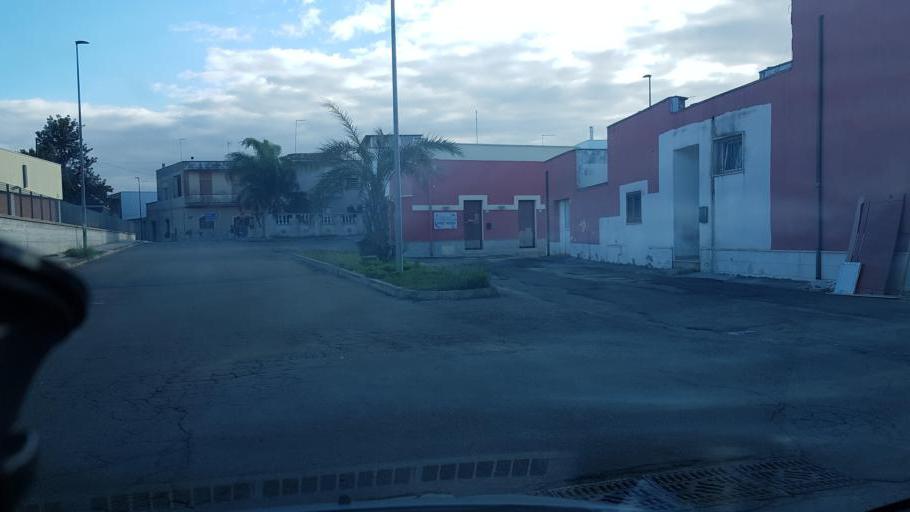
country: IT
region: Apulia
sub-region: Provincia di Lecce
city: Guagnano
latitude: 40.4020
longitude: 17.9549
